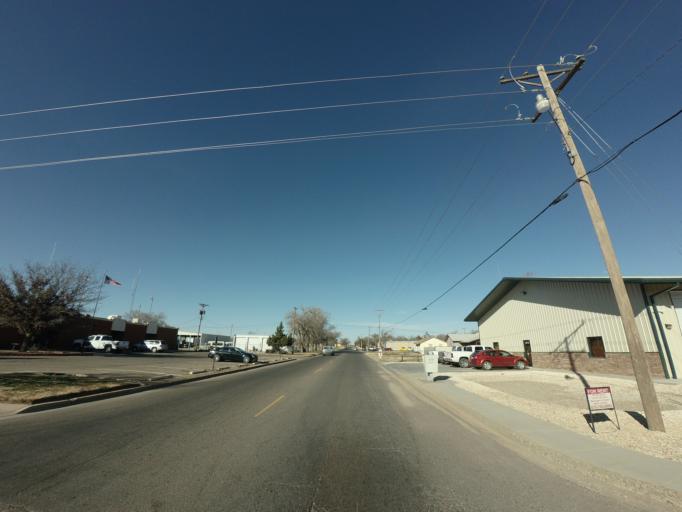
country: US
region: New Mexico
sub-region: Curry County
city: Clovis
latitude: 34.4029
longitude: -103.1877
